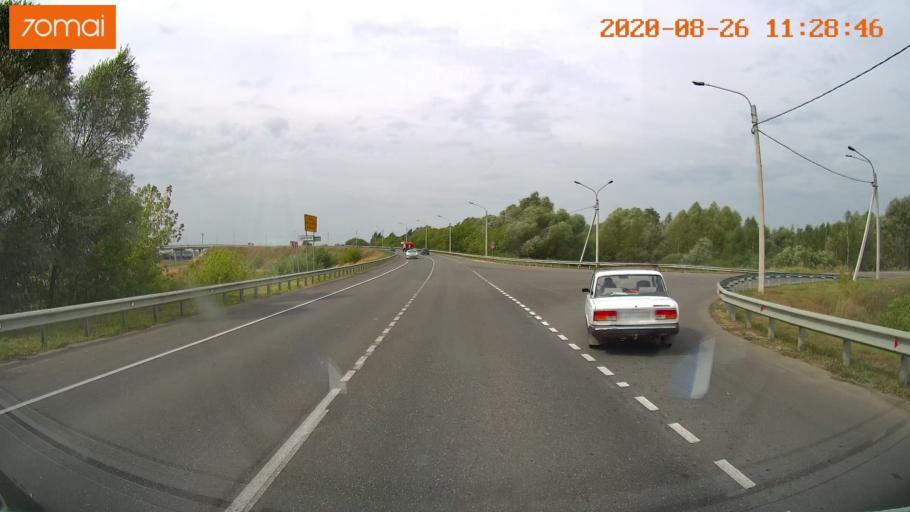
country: RU
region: Rjazan
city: Shilovo
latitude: 54.3232
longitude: 40.9065
